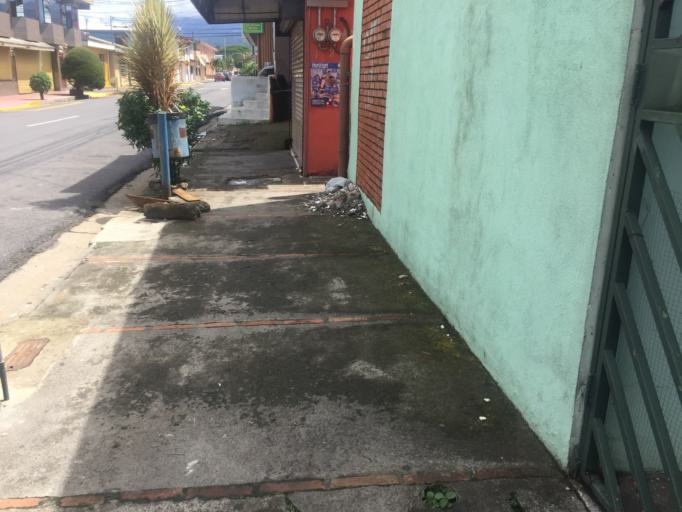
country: CR
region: Heredia
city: Heredia
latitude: 10.0018
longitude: -84.1192
